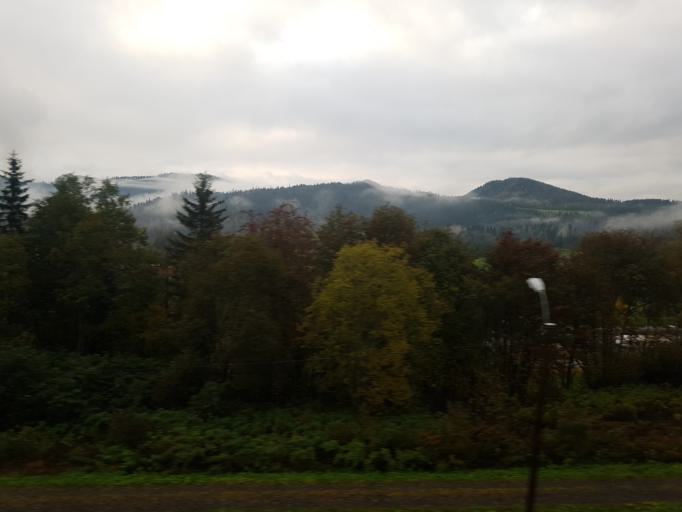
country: NO
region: Sor-Trondelag
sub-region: Midtre Gauldal
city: Storen
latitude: 63.0389
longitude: 10.2797
